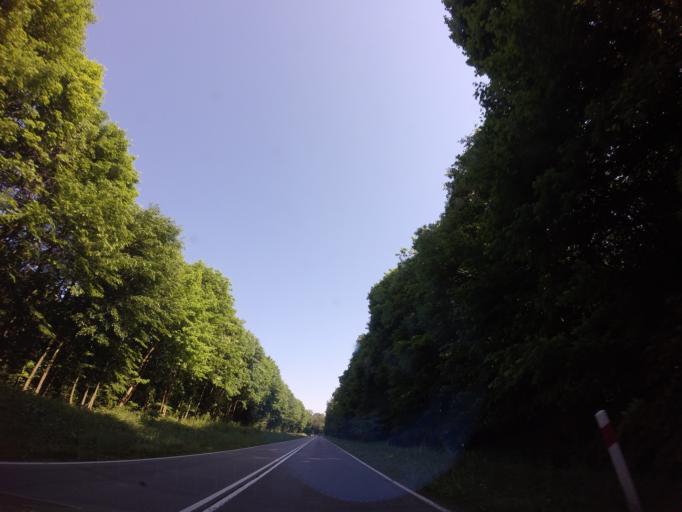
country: PL
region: West Pomeranian Voivodeship
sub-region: Powiat gryfinski
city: Stare Czarnowo
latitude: 53.3284
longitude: 14.7825
